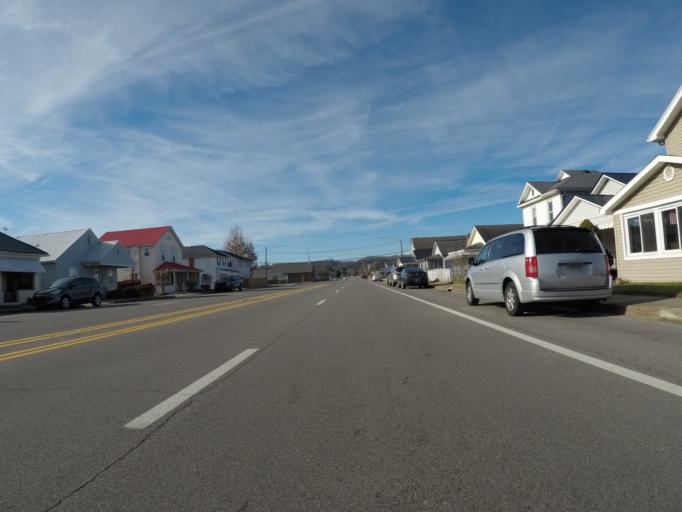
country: US
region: West Virginia
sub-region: Wayne County
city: Kenova
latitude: 38.4015
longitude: -82.5787
